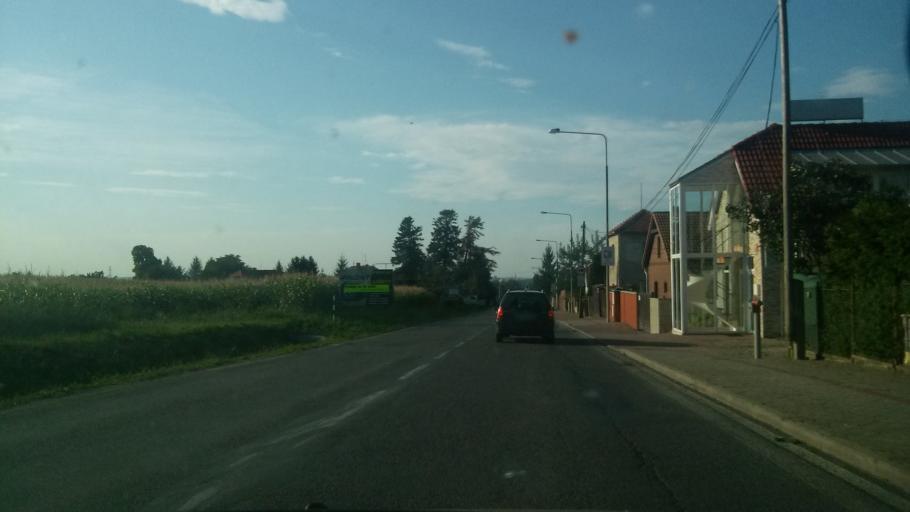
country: CZ
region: Central Bohemia
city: Vestec
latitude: 49.9758
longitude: 14.5009
